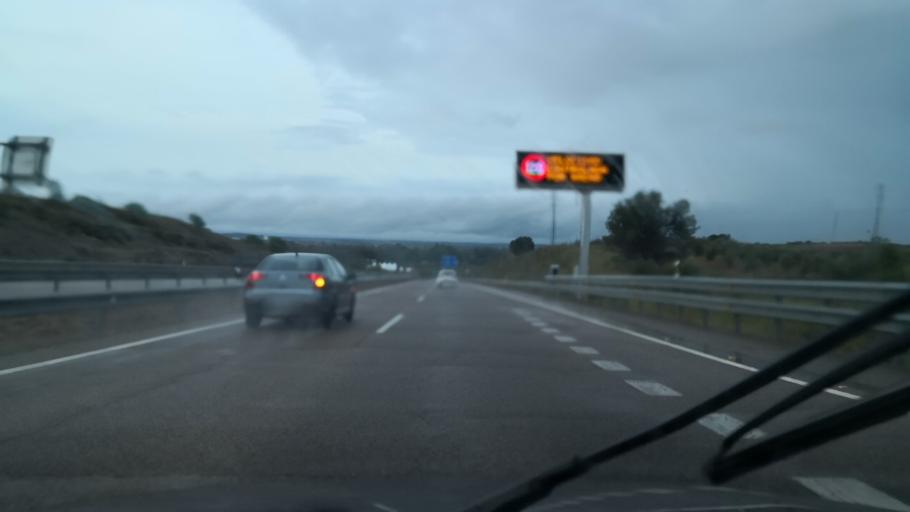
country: ES
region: Extremadura
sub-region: Provincia de Badajoz
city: Lobon
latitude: 38.8471
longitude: -6.6172
